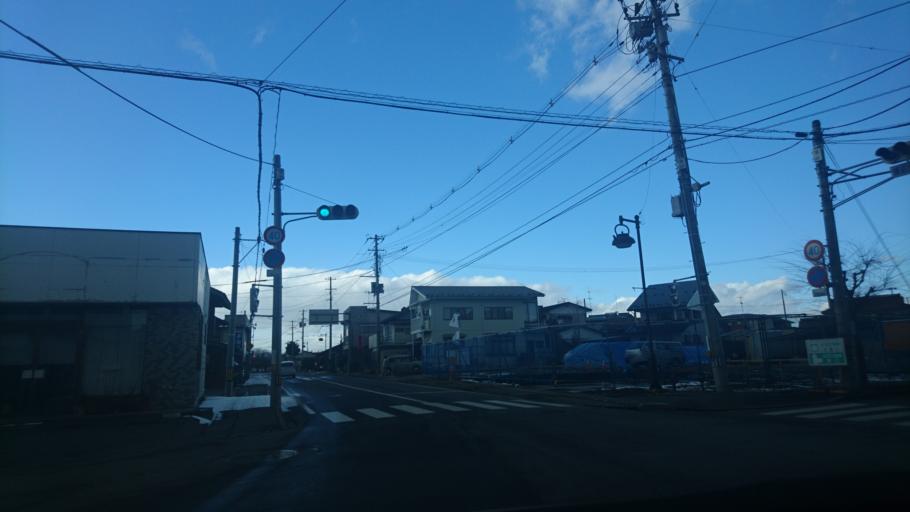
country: JP
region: Iwate
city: Mizusawa
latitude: 39.1430
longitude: 141.1870
